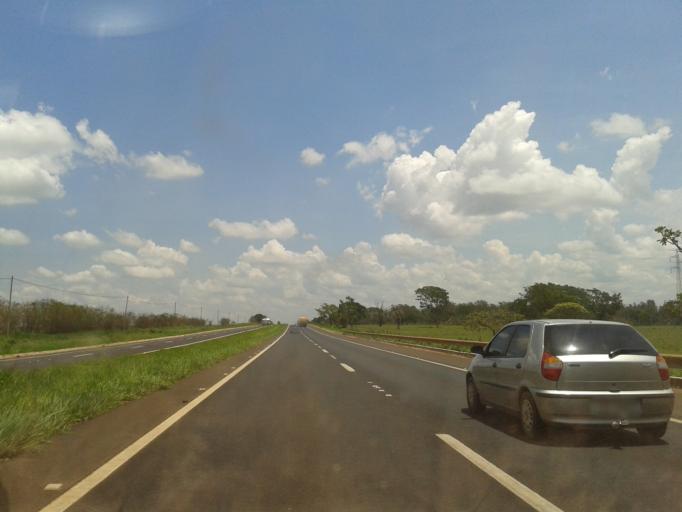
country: BR
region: Minas Gerais
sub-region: Uberlandia
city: Uberlandia
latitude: -18.8784
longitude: -48.5078
